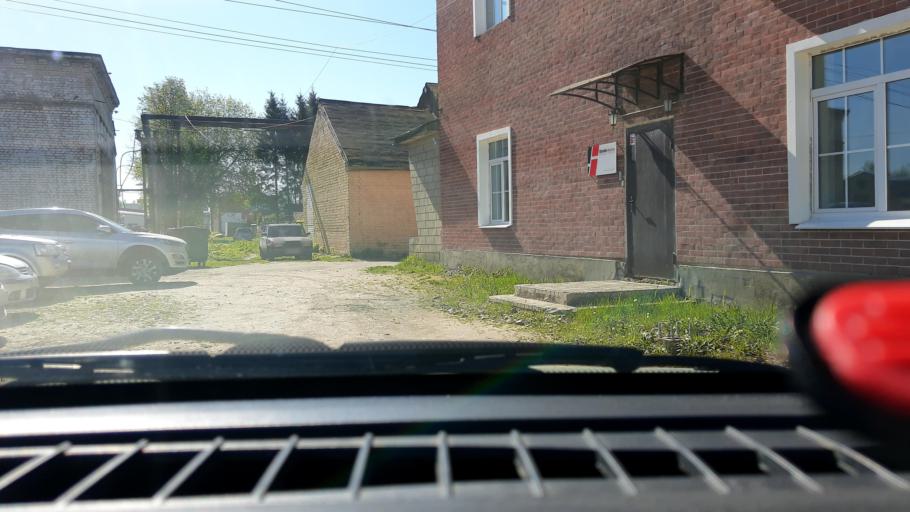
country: RU
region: Nizjnij Novgorod
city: Neklyudovo
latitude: 56.3554
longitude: 43.8688
